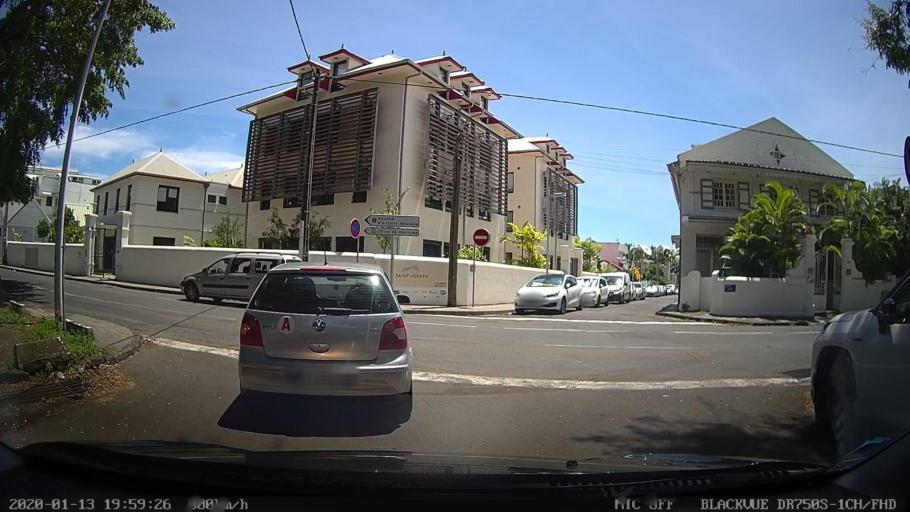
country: RE
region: Reunion
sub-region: Reunion
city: Saint-Denis
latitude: -20.8877
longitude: 55.4523
